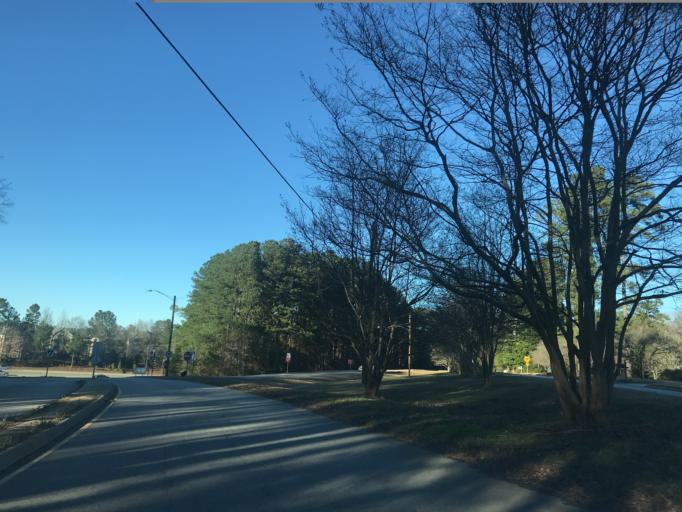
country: US
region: North Carolina
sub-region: Wake County
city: West Raleigh
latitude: 35.8316
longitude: -78.6741
